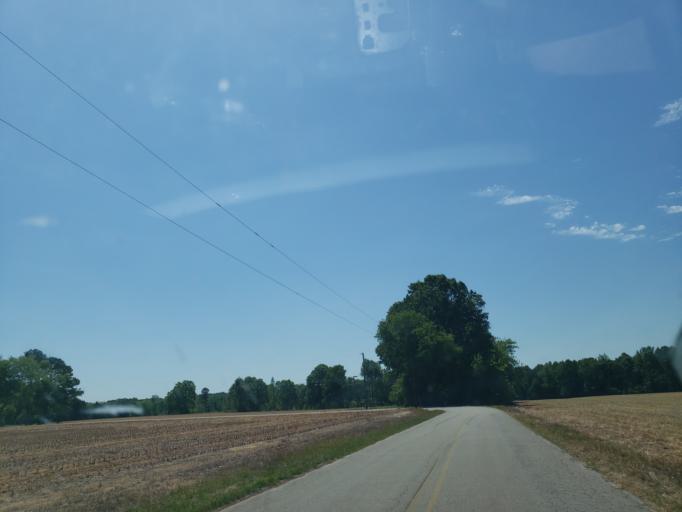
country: US
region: Alabama
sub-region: Madison County
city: Hazel Green
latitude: 34.9444
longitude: -86.5355
